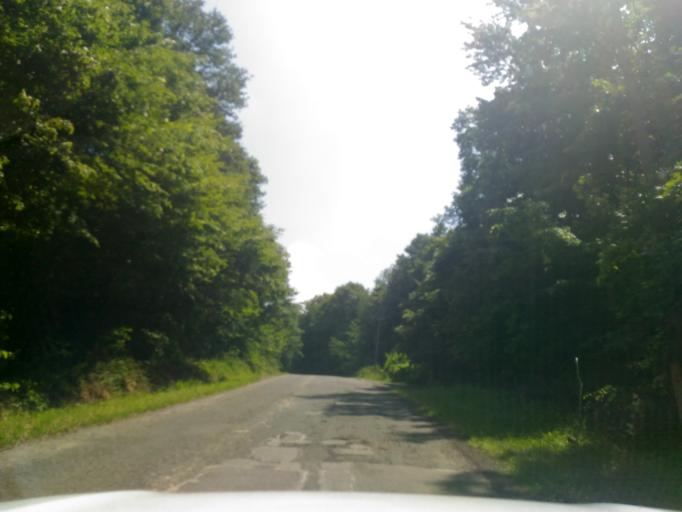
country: HU
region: Baranya
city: Pecs
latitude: 46.1346
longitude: 18.2481
